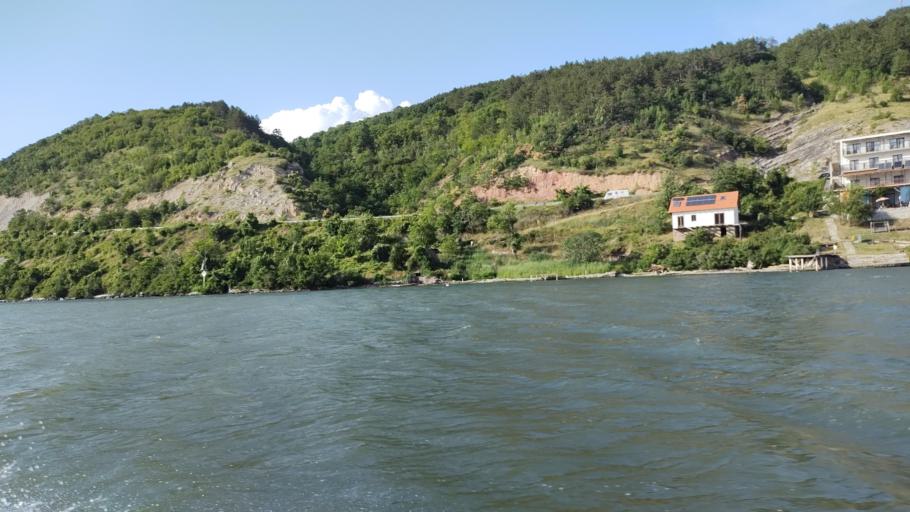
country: RO
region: Mehedinti
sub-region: Comuna Svinita
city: Svinita
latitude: 44.5008
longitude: 22.0875
